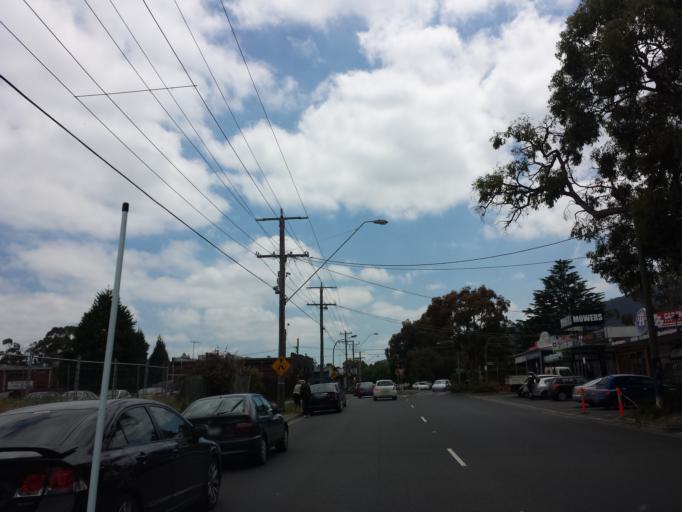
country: AU
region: Victoria
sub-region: Knox
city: Ferntree Gully
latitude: -37.8837
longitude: 145.2968
